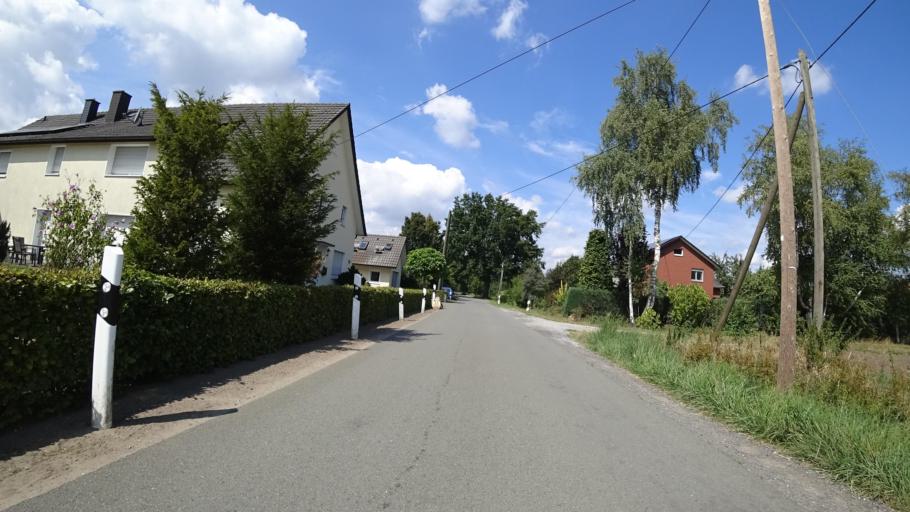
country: DE
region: North Rhine-Westphalia
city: Rietberg
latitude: 51.8738
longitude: 8.4399
